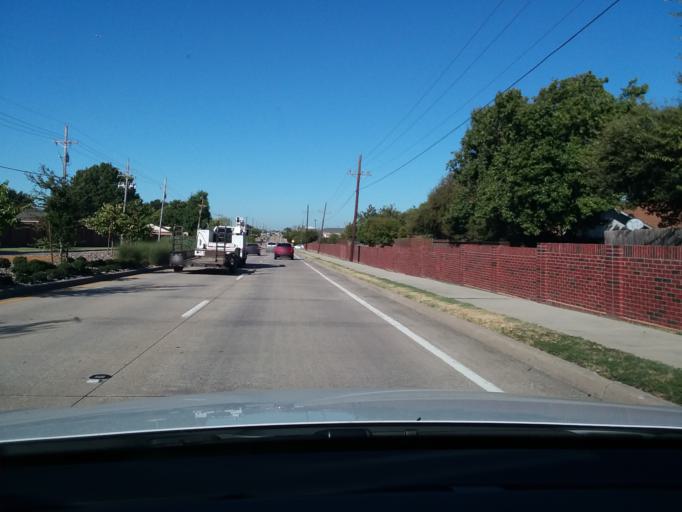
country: US
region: Texas
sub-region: Denton County
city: Highland Village
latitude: 33.0716
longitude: -97.0419
